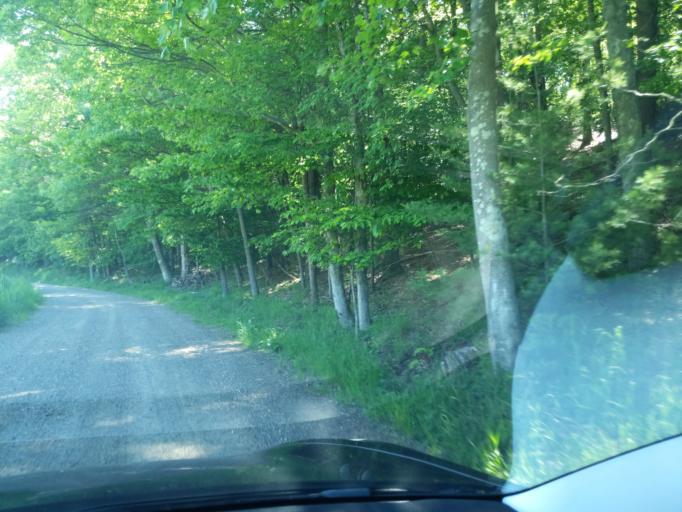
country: US
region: Michigan
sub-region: Muskegon County
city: Montague
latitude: 43.3857
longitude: -86.4248
